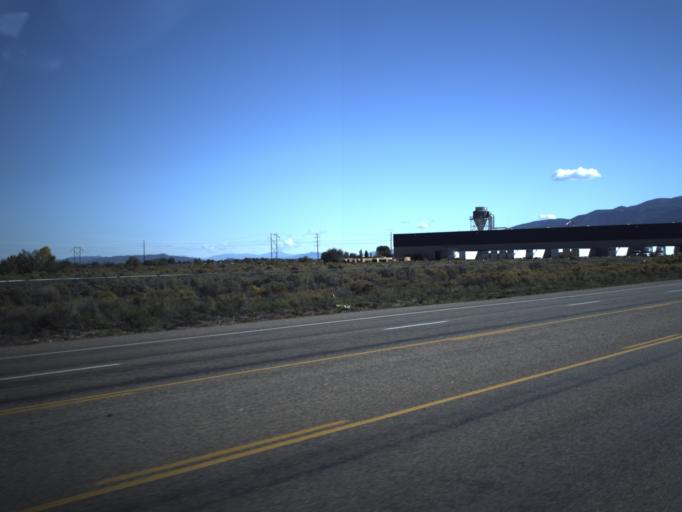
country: US
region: Utah
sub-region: Iron County
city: Cedar City
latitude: 37.6849
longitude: -113.1538
